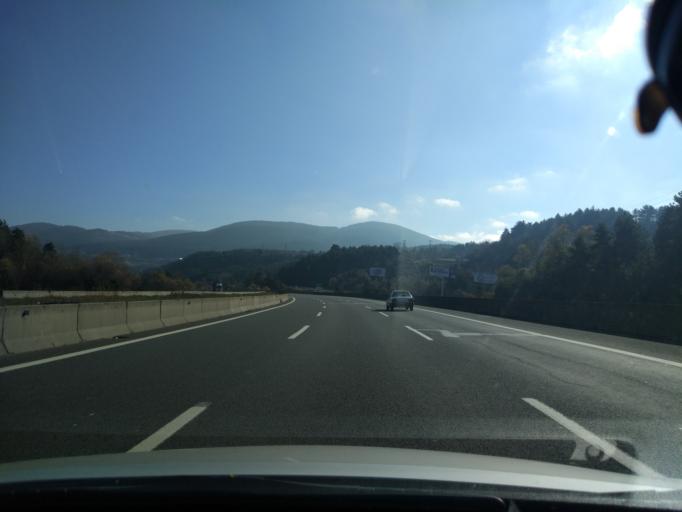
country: TR
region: Bolu
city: Bolu
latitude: 40.7431
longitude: 31.7836
